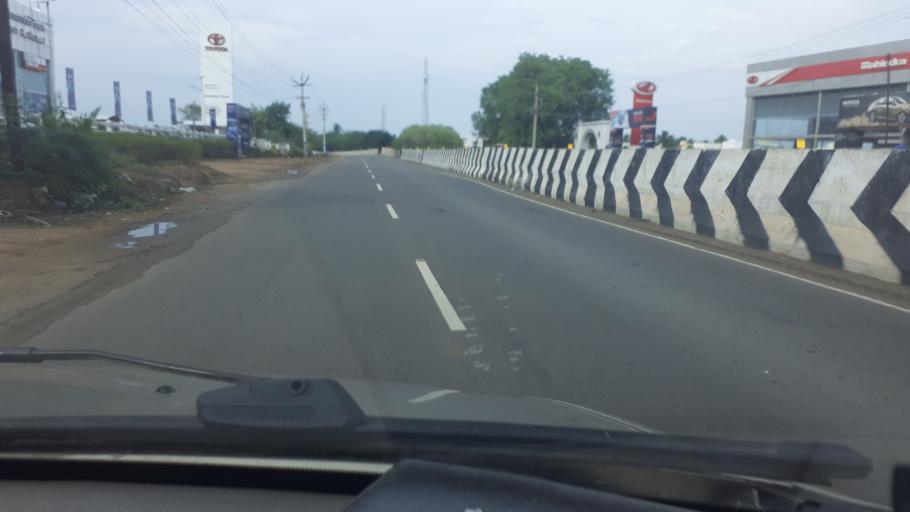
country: IN
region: Tamil Nadu
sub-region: Tirunelveli Kattabo
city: Tirunelveli
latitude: 8.6682
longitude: 77.7175
